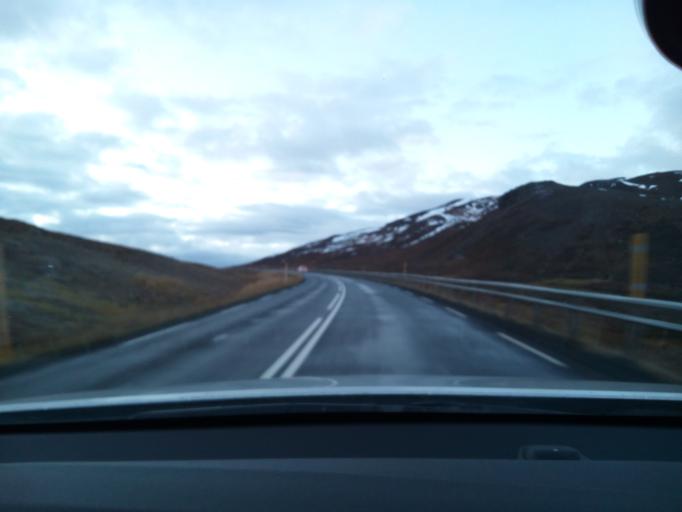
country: IS
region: Northeast
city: Akureyri
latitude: 65.8018
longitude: -17.9508
